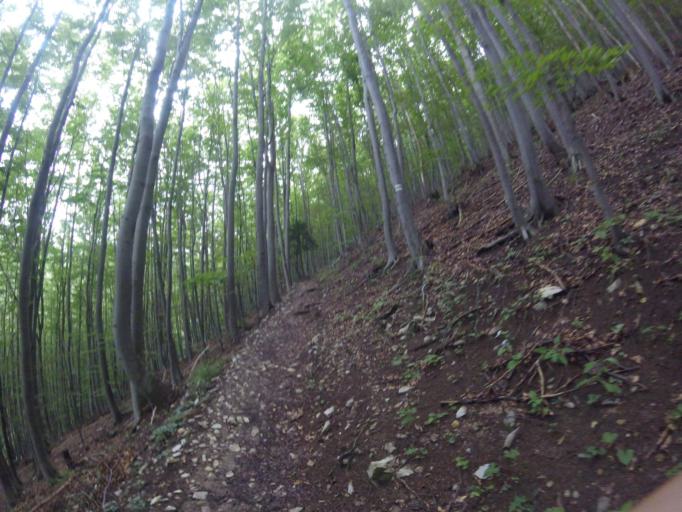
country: SK
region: Zilinsky
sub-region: Okres Zilina
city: Terchova
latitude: 49.2360
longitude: 19.0312
